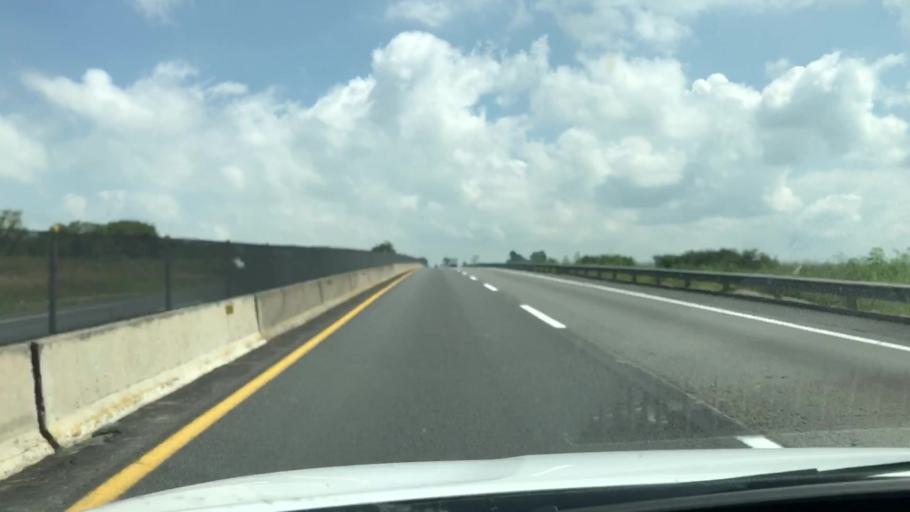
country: MX
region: Jalisco
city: Valle de Guadalupe
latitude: 20.9924
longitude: -102.5971
